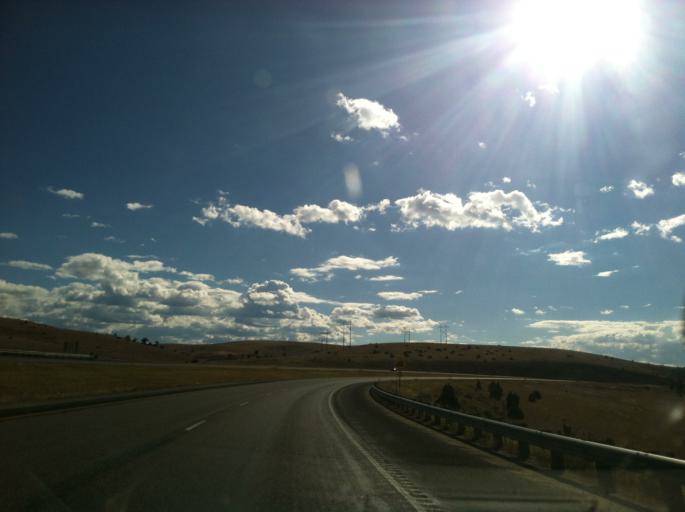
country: US
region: Montana
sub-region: Jefferson County
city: Whitehall
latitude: 45.8807
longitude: -111.8726
